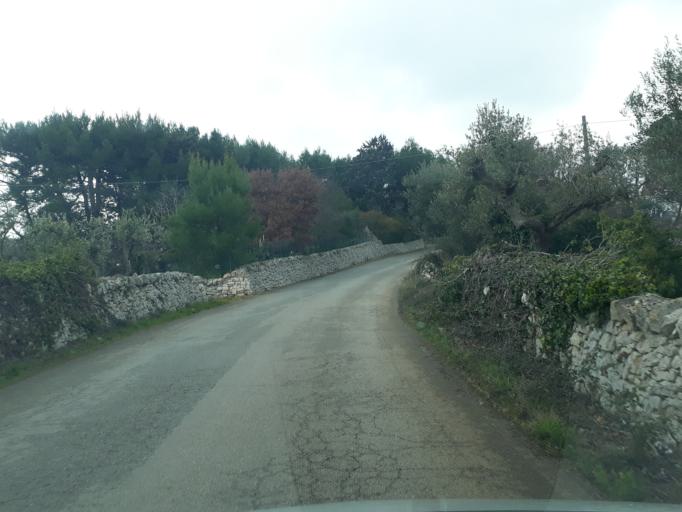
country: IT
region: Apulia
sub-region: Provincia di Brindisi
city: Lamie di Olimpie-Selva
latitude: 40.7921
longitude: 17.3367
